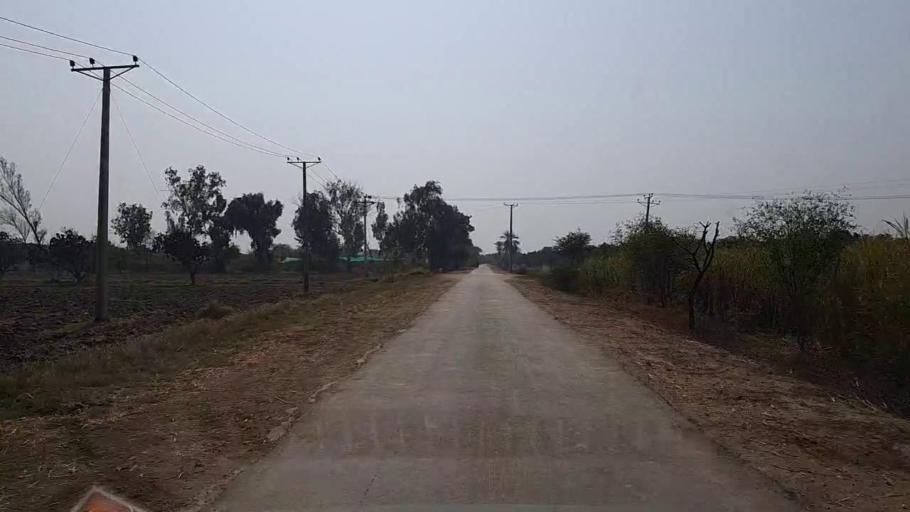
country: PK
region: Sindh
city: Mirwah Gorchani
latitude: 25.3233
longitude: 69.0024
